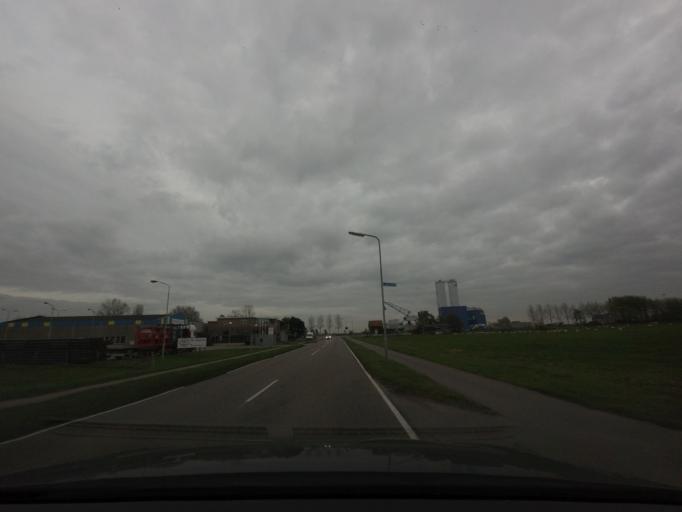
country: NL
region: North Holland
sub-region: Gemeente Alkmaar
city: Alkmaar
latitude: 52.5891
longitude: 4.7514
